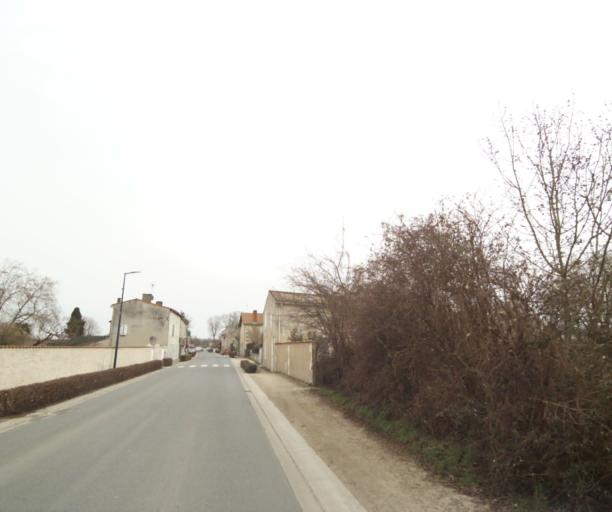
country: FR
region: Poitou-Charentes
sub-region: Departement des Deux-Sevres
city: Magne
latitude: 46.3113
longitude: -0.5285
